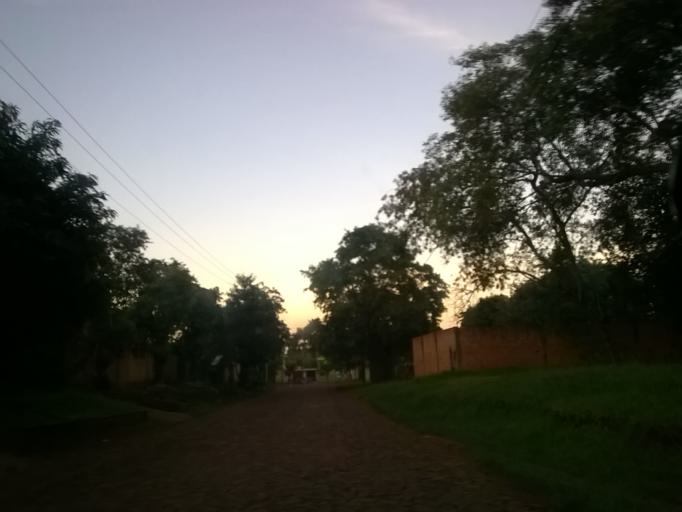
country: PY
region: Alto Parana
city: Ciudad del Este
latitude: -25.4782
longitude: -54.6480
